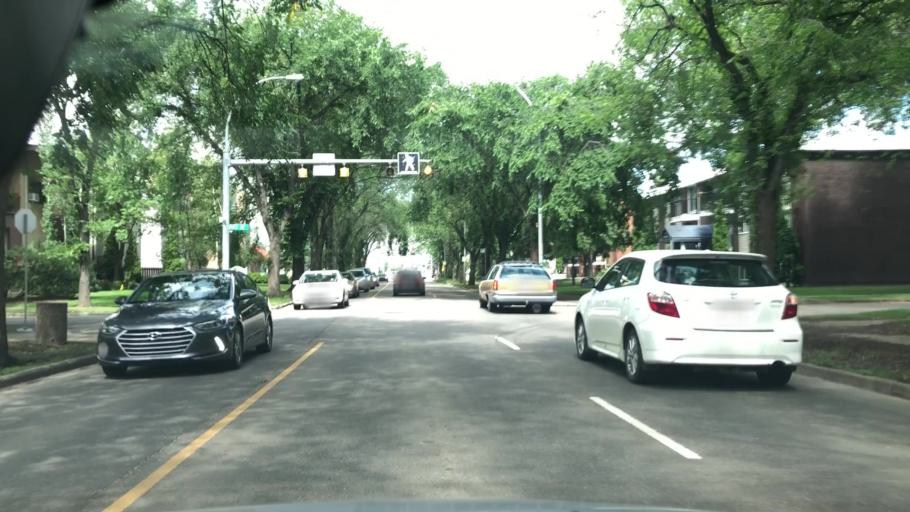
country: CA
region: Alberta
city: Edmonton
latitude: 53.5443
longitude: -113.5213
